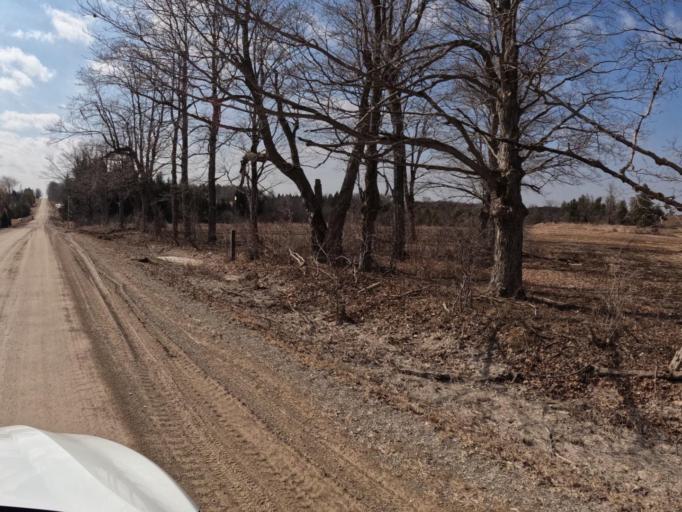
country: CA
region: Ontario
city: Orangeville
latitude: 43.9028
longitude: -80.2514
